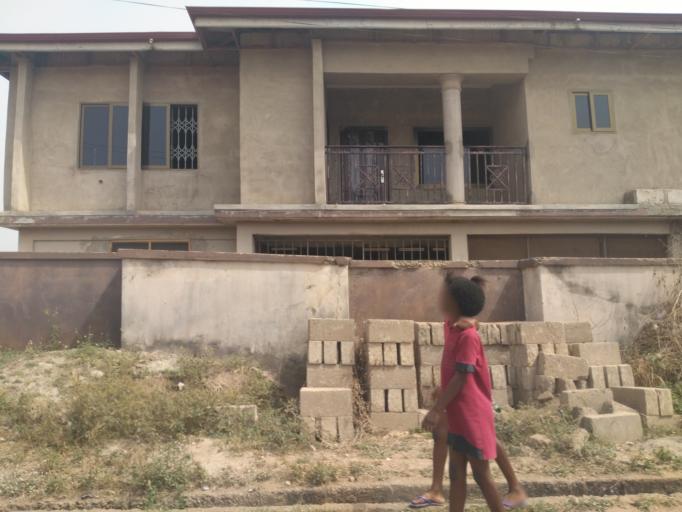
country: GH
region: Ashanti
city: Kumasi
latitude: 6.6828
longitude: -1.5992
